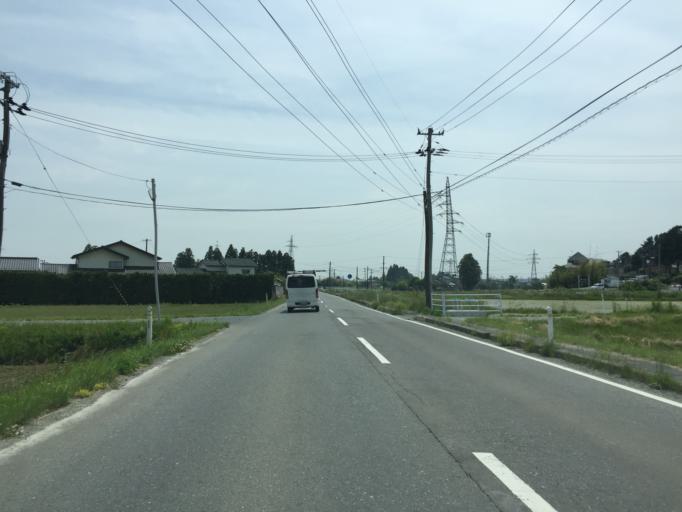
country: JP
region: Fukushima
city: Namie
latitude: 37.6294
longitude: 140.9360
